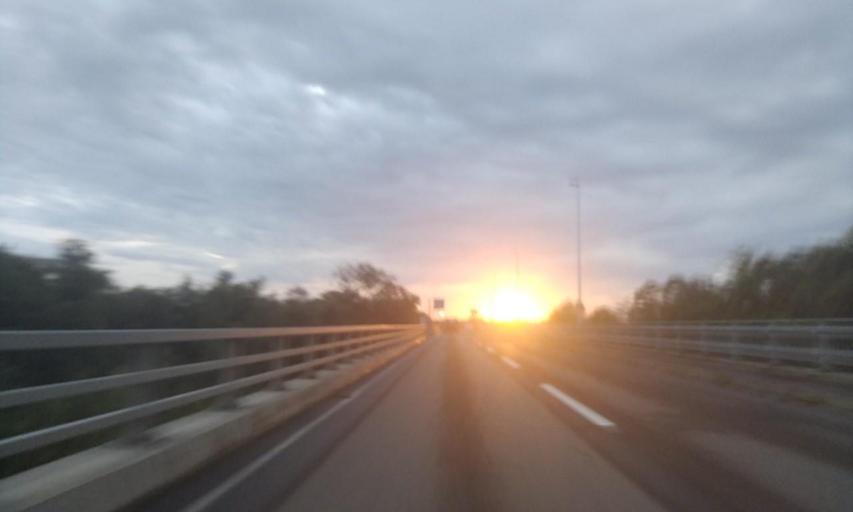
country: JP
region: Hokkaido
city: Abashiri
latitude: 43.8998
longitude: 144.6419
